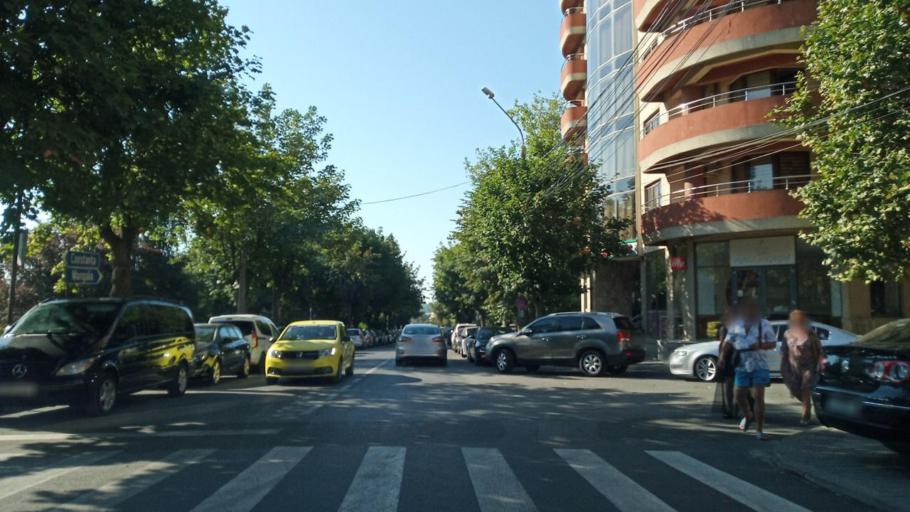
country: RO
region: Constanta
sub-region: Oras Eforie
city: Eforie Nord
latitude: 44.0619
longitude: 28.6352
